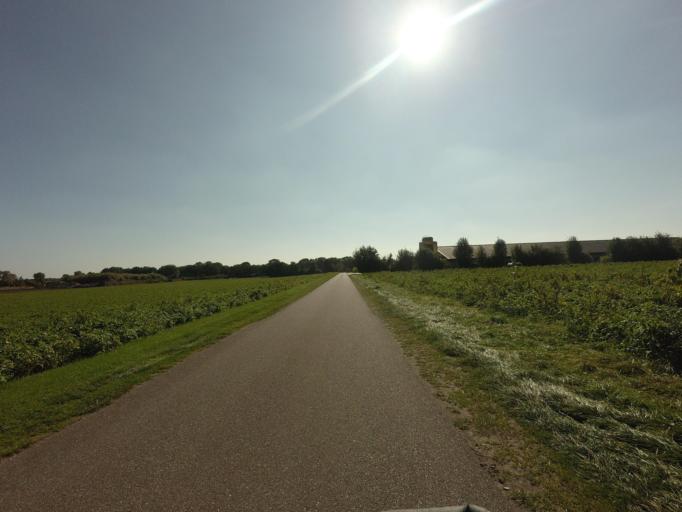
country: DE
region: Lower Saxony
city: Wielen
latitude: 52.5242
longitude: 6.7081
